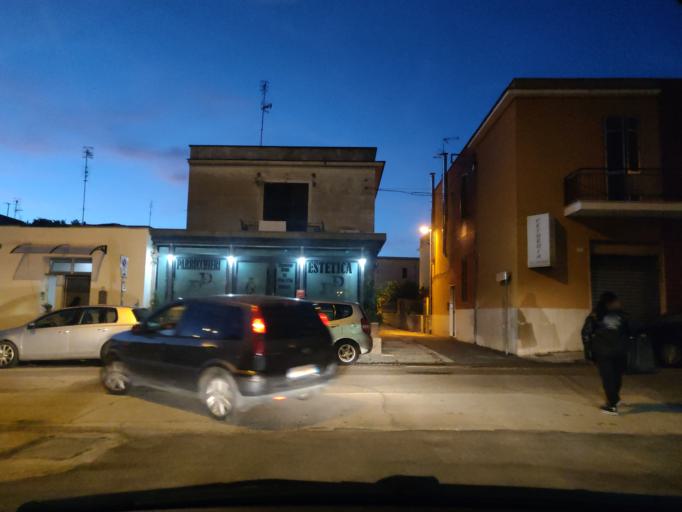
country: IT
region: Latium
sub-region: Citta metropolitana di Roma Capitale
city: Civitavecchia
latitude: 42.0895
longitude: 11.8063
